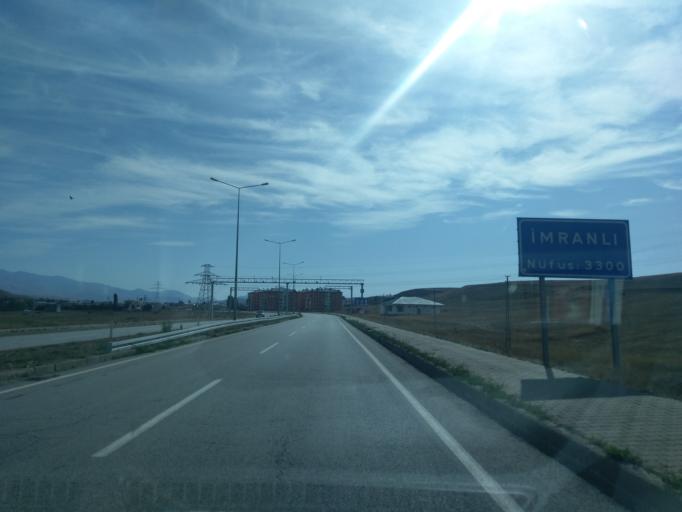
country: TR
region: Sivas
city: Imranli
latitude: 39.8712
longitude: 38.0974
